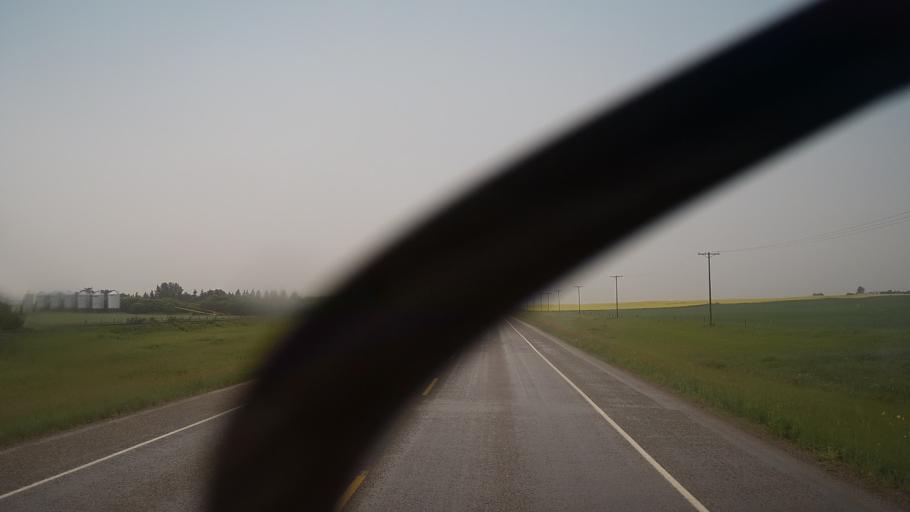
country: CA
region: Saskatchewan
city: Biggar
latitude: 52.1375
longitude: -108.1748
